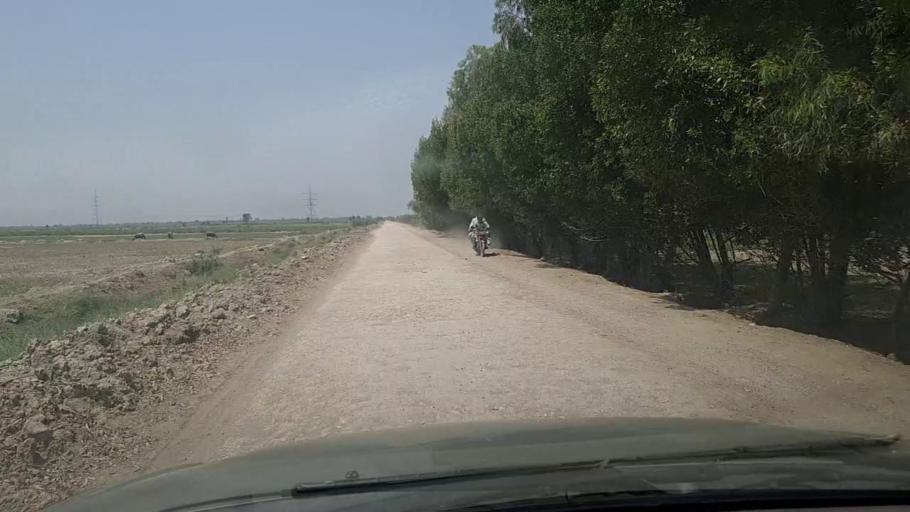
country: PK
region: Sindh
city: Adilpur
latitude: 27.9385
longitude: 69.2982
